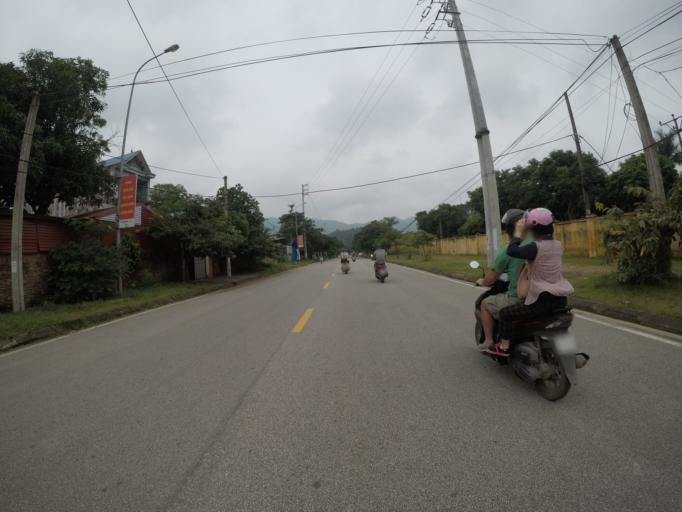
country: VN
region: Ha Noi
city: Soc Son
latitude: 21.2821
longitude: 105.8425
